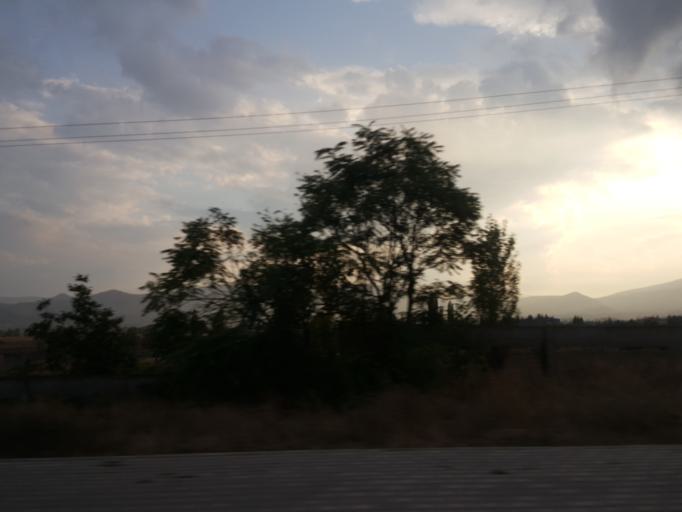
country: TR
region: Amasya
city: Gumushacikoy
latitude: 40.8761
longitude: 35.2342
